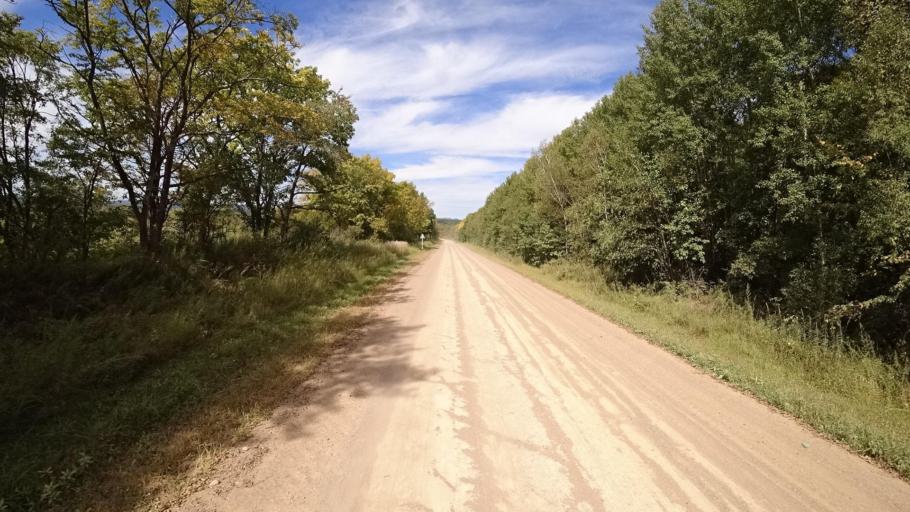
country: RU
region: Primorskiy
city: Yakovlevka
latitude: 44.6304
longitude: 133.6013
